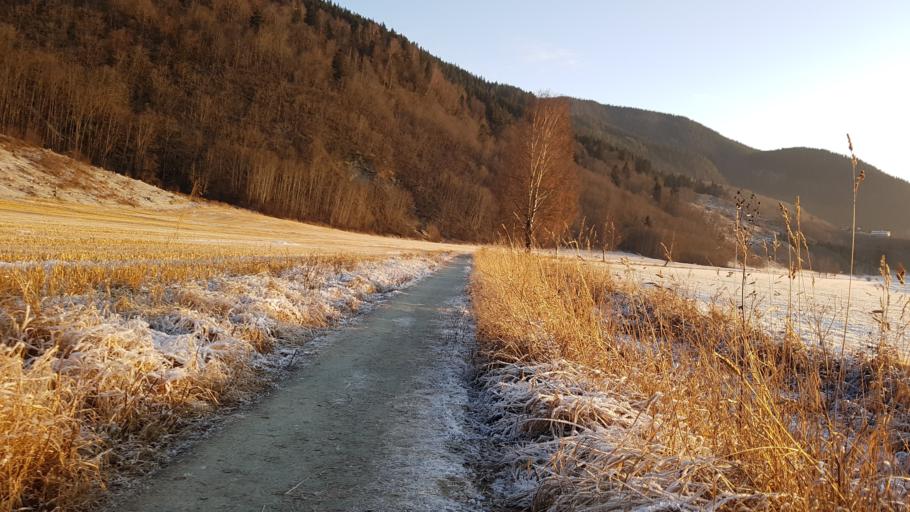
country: NO
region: Sor-Trondelag
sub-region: Melhus
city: Melhus
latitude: 63.2830
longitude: 10.2993
